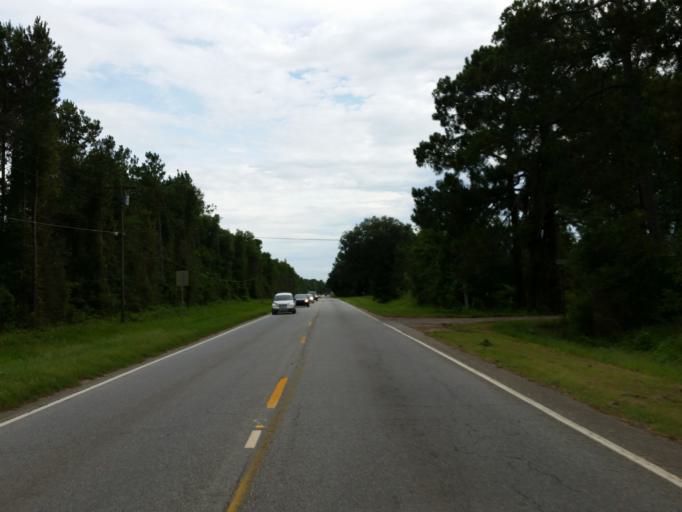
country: US
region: Georgia
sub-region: Lowndes County
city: Valdosta
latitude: 30.7402
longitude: -83.2791
